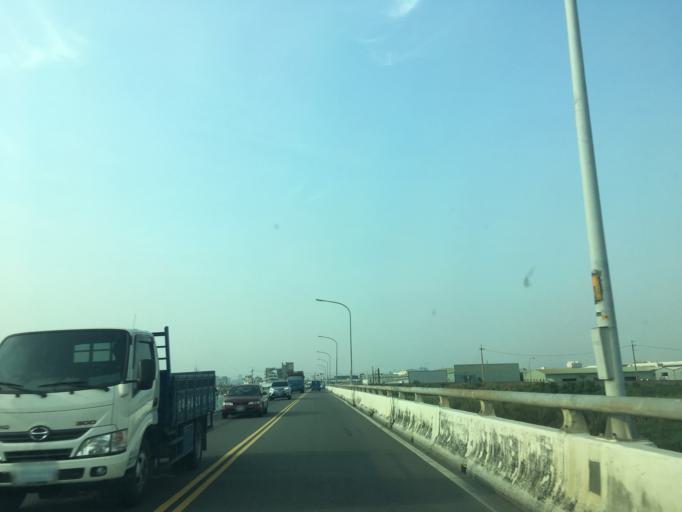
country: TW
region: Taiwan
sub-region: Taichung City
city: Taichung
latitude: 24.0717
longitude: 120.6800
